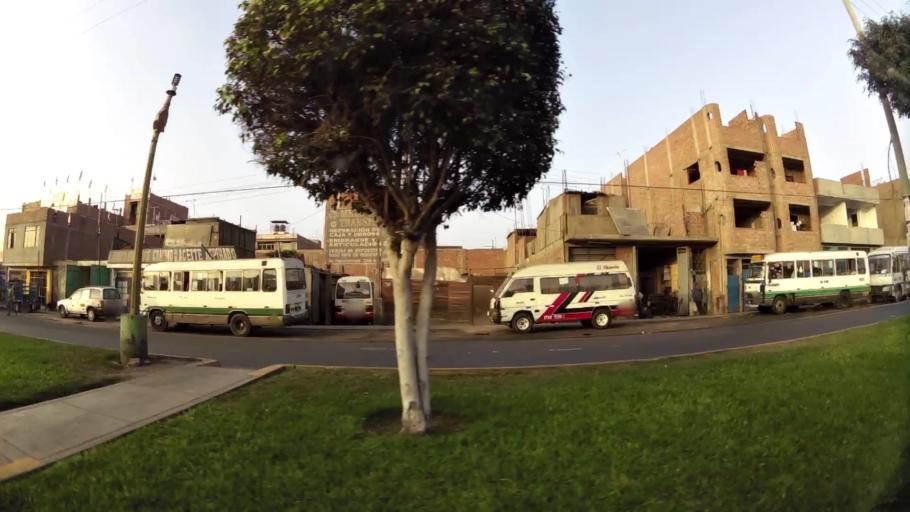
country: PE
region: Callao
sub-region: Callao
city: Callao
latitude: -12.0018
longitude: -77.1058
